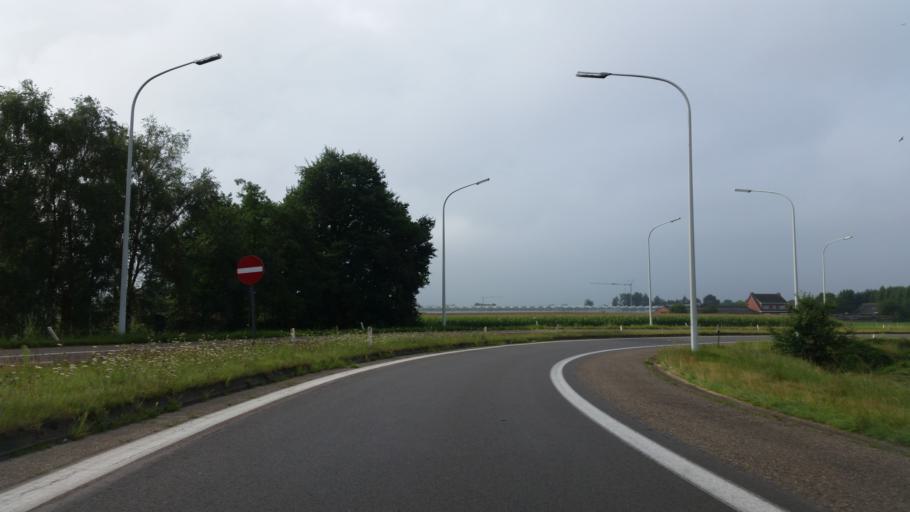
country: BE
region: Flanders
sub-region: Provincie Antwerpen
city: Hoogstraten
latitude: 51.4517
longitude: 4.7235
